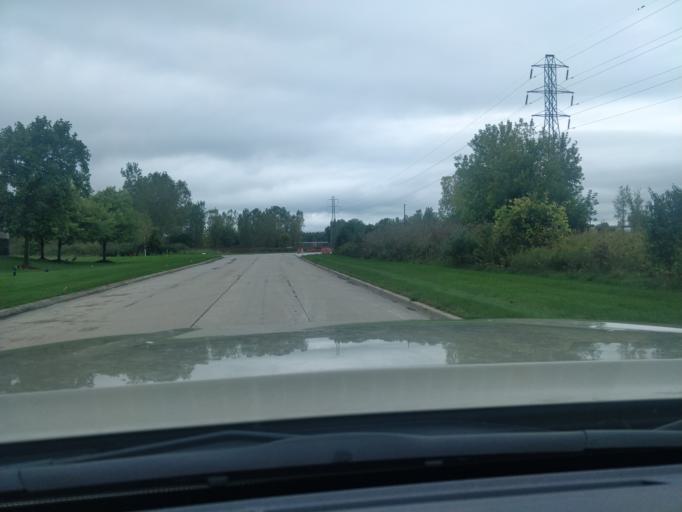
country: US
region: Michigan
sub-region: Wayne County
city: Romulus
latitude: 42.1758
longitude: -83.3899
